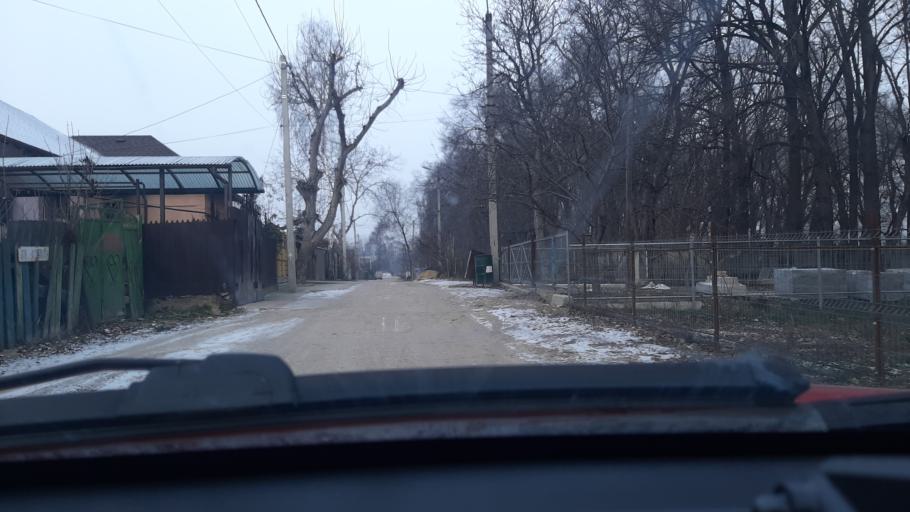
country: MD
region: Chisinau
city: Chisinau
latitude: 46.9870
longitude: 28.8940
